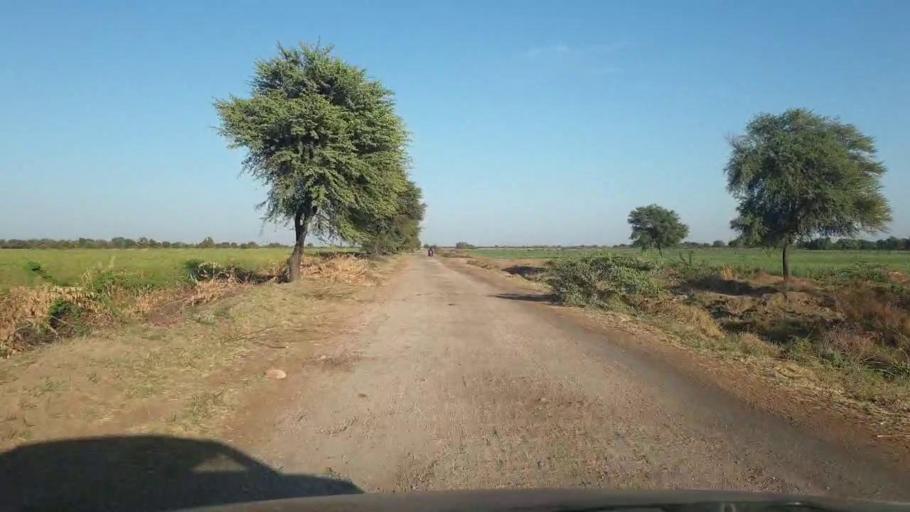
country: PK
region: Sindh
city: Dhoro Naro
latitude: 25.3923
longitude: 69.5774
